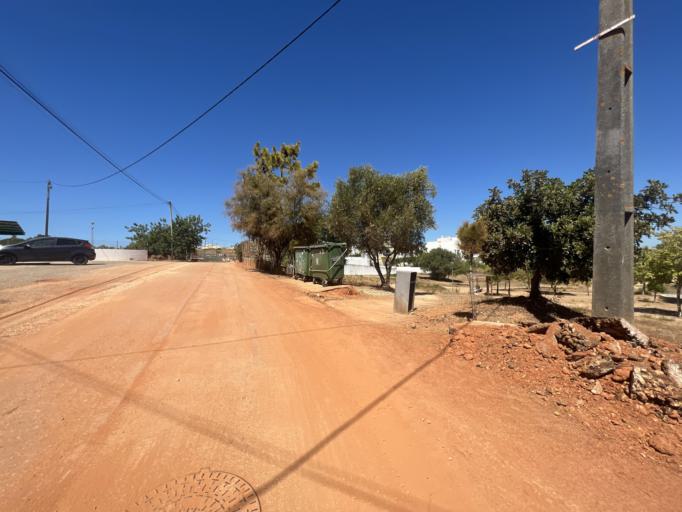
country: PT
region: Faro
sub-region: Portimao
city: Portimao
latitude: 37.1312
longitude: -8.5108
